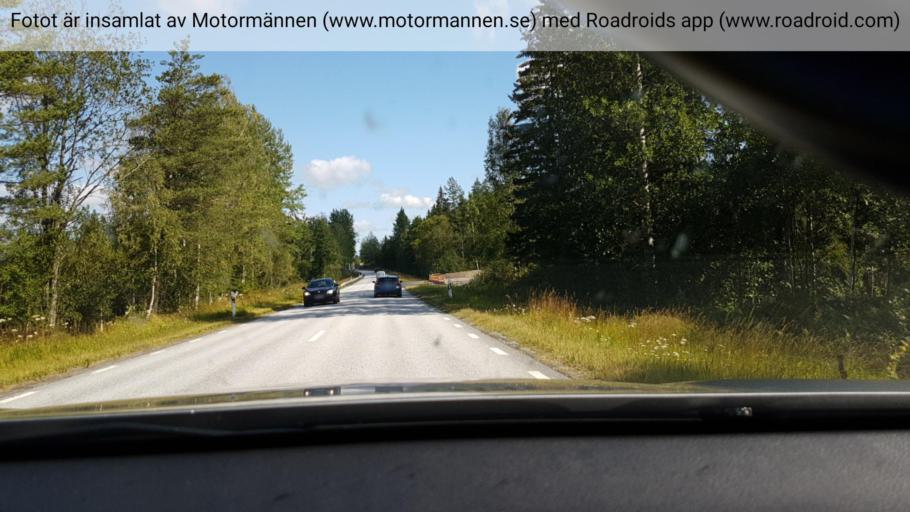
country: SE
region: Stockholm
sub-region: Norrtalje Kommun
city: Norrtalje
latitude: 59.7069
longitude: 18.6657
